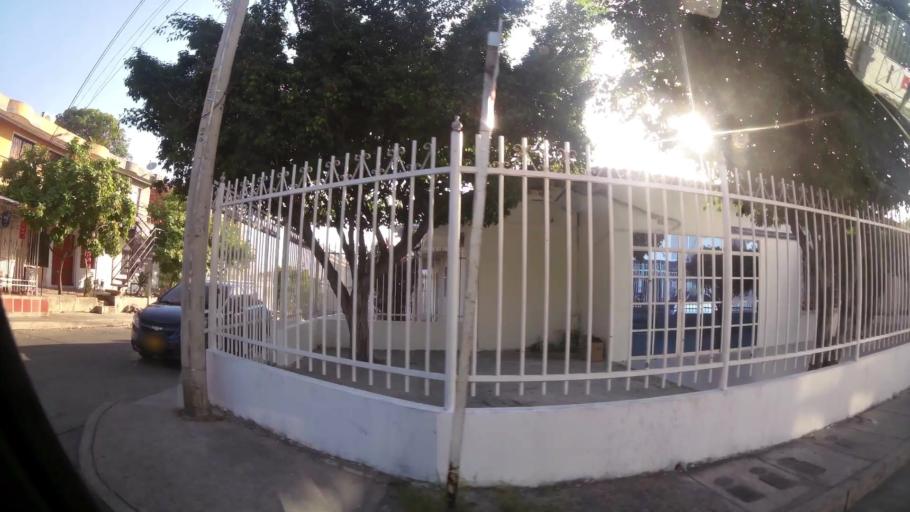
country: CO
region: Bolivar
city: Cartagena
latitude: 10.4055
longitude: -75.5184
